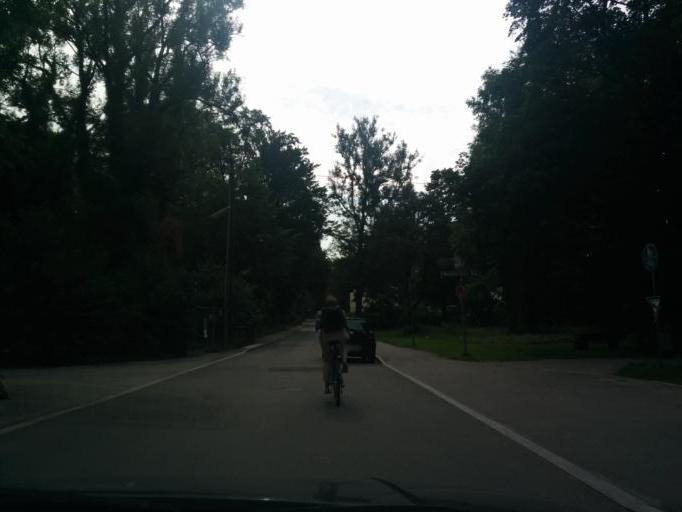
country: DE
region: Bavaria
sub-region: Upper Bavaria
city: Pullach im Isartal
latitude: 48.0954
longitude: 11.5428
